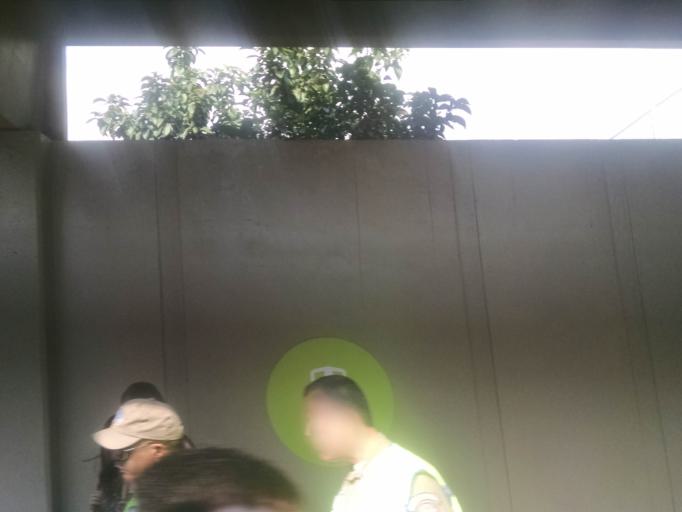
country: BR
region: Rio de Janeiro
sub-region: Rio De Janeiro
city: Rio de Janeiro
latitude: -22.9097
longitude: -43.2215
